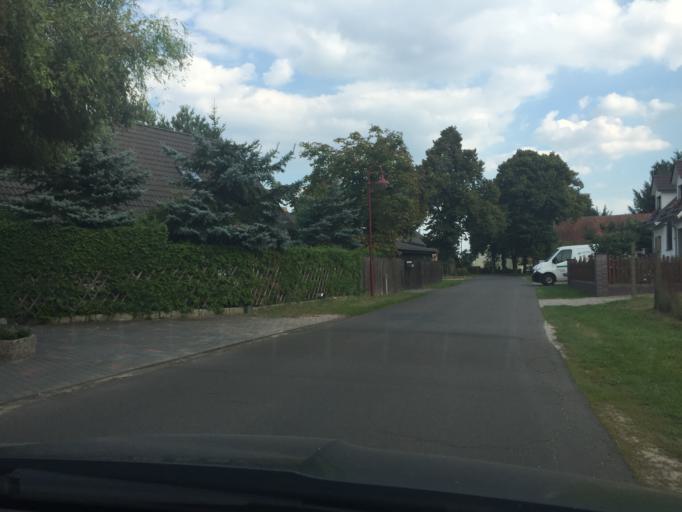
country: DE
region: Brandenburg
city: Spreenhagen
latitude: 52.3546
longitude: 13.8296
